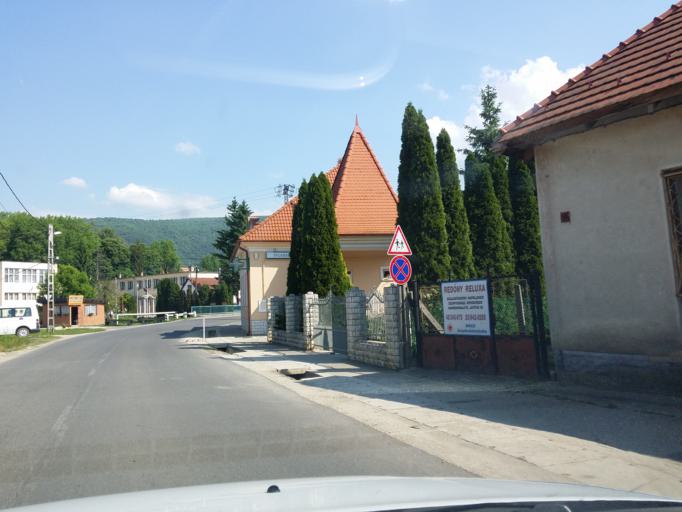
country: HU
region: Borsod-Abauj-Zemplen
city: Szendro
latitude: 48.5351
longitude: 20.7322
